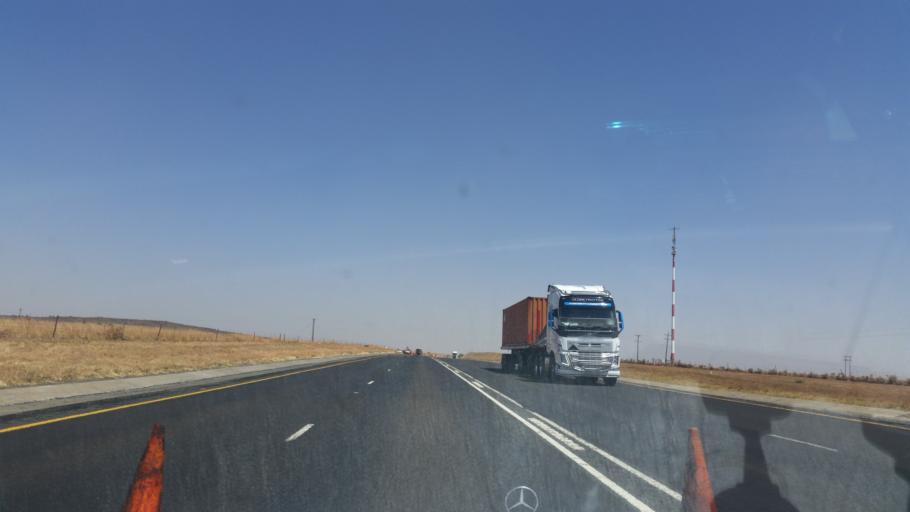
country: ZA
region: Orange Free State
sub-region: Lejweleputswa District Municipality
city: Brandfort
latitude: -28.8120
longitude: 26.6732
